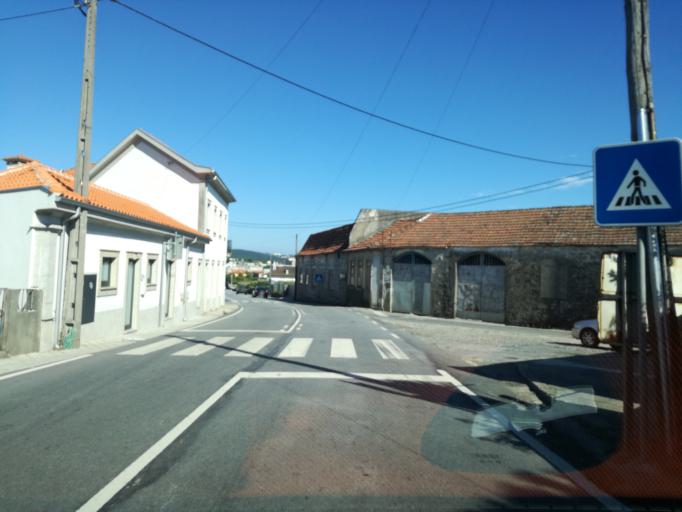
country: PT
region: Porto
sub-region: Trofa
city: Sao Romao do Coronado
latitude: 41.2838
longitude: -8.5752
